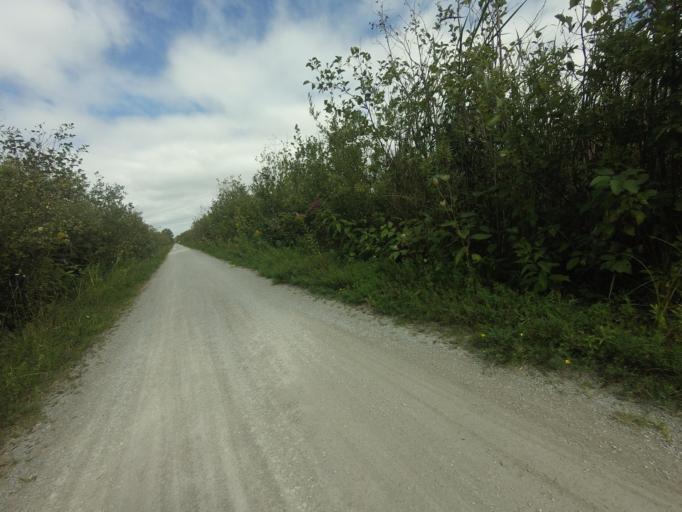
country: CA
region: Ontario
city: Uxbridge
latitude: 44.1752
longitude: -79.0737
